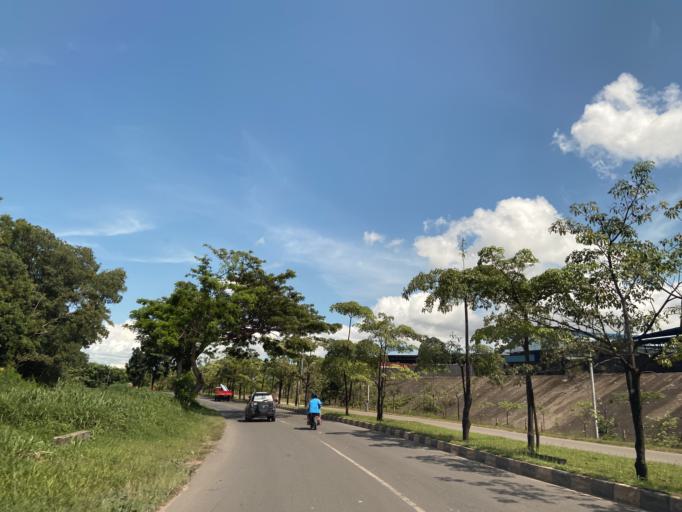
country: SG
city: Singapore
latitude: 1.1129
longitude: 104.0580
